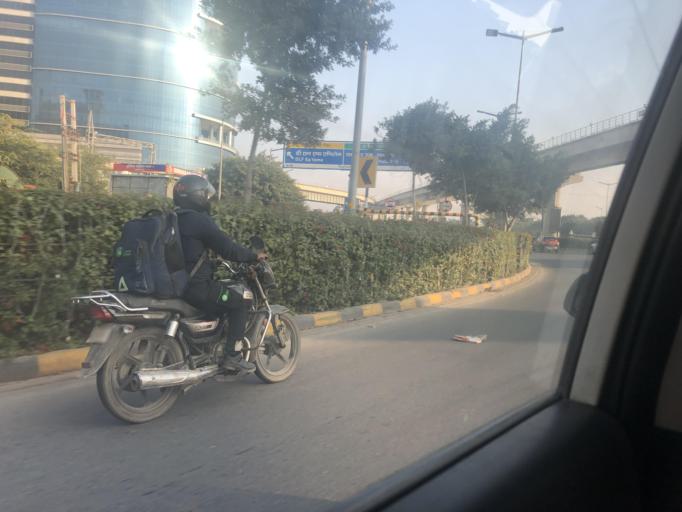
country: IN
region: Haryana
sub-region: Gurgaon
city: Gurgaon
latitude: 28.4897
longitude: 77.0900
